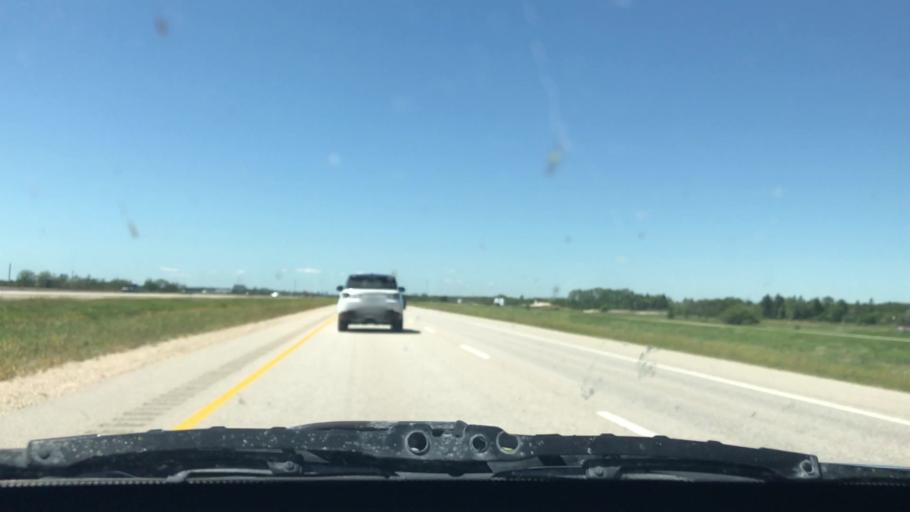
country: CA
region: Manitoba
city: Niverville
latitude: 49.8074
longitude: -96.9046
